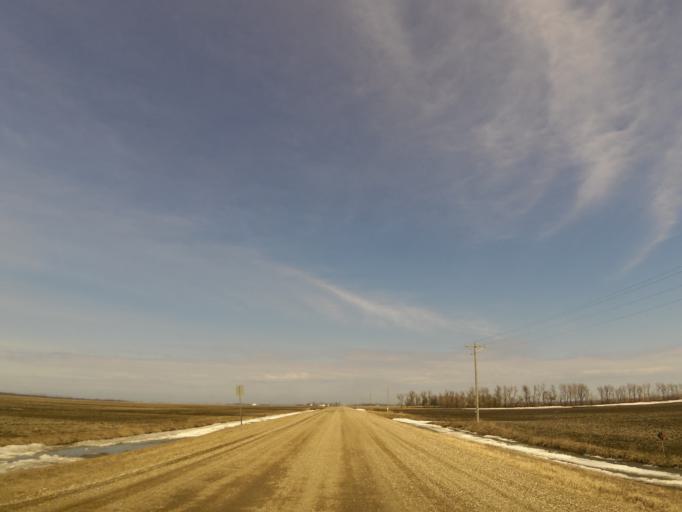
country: US
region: North Dakota
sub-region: Walsh County
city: Grafton
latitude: 48.3001
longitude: -97.2549
